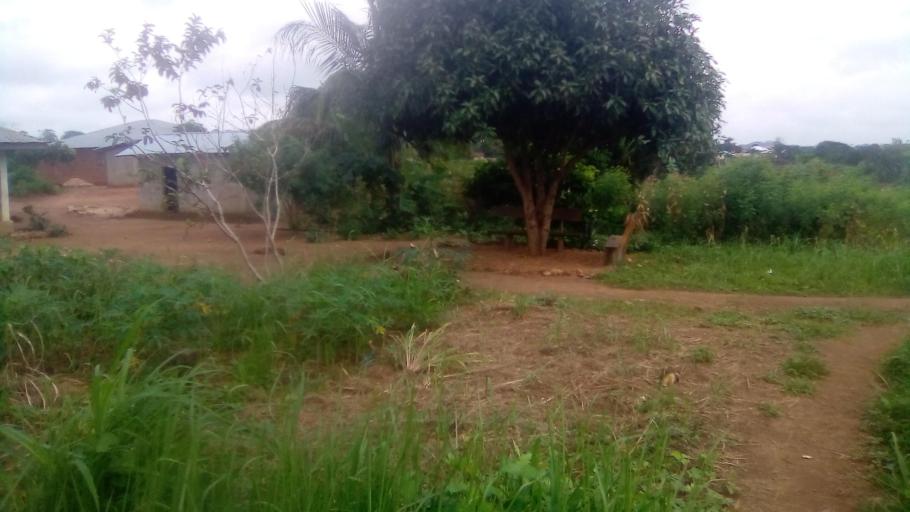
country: SL
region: Eastern Province
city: Kailahun
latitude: 8.2703
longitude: -10.5666
